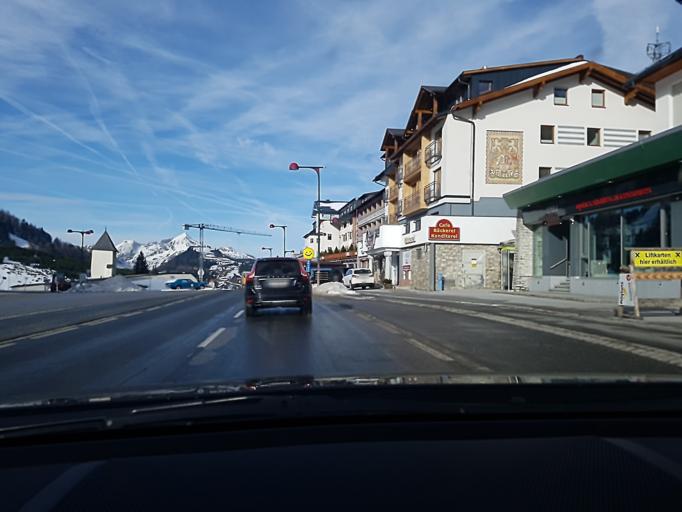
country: AT
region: Salzburg
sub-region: Politischer Bezirk Sankt Johann im Pongau
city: Untertauern
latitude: 47.2486
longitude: 13.5580
